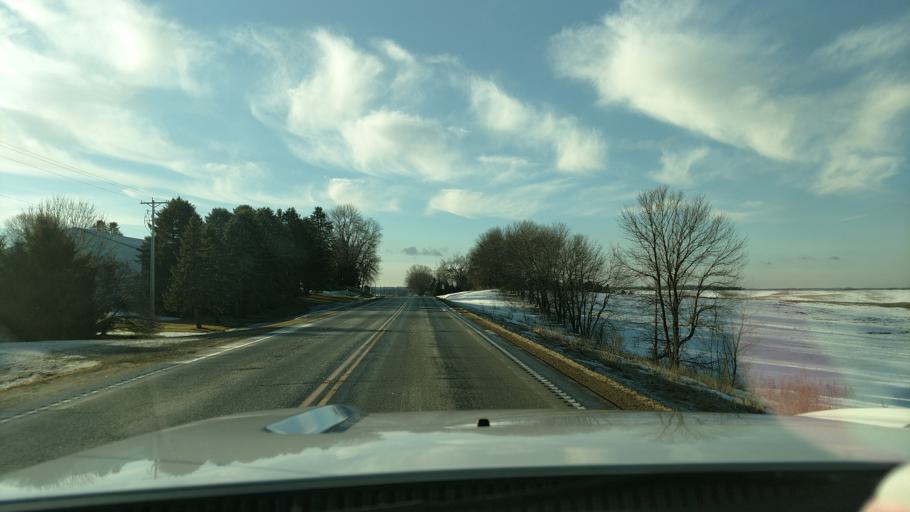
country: US
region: Minnesota
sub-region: Wabasha County
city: Lake City
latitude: 44.3299
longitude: -92.4109
